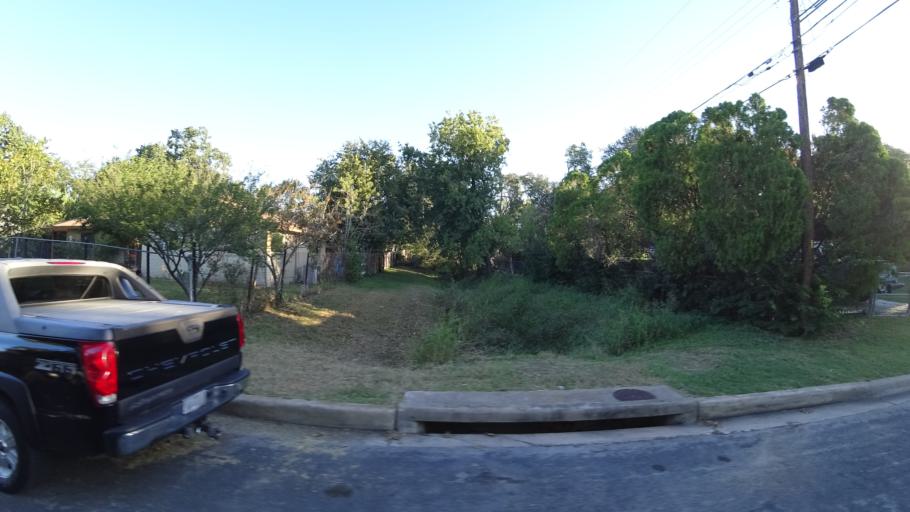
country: US
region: Texas
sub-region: Travis County
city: Austin
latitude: 30.3030
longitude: -97.6801
